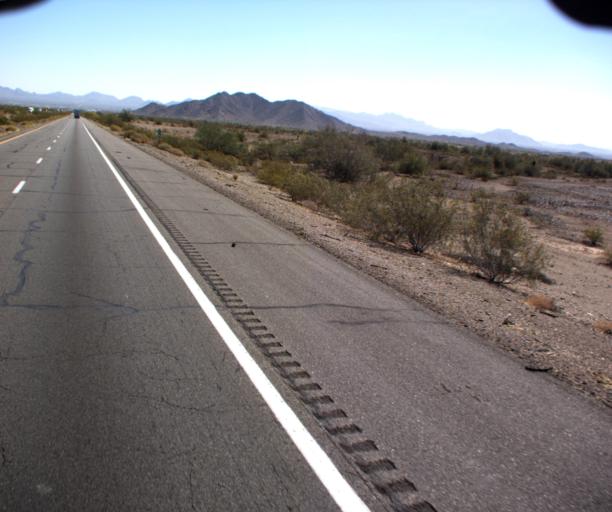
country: US
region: Arizona
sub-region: La Paz County
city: Quartzsite
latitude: 33.6509
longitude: -114.3016
